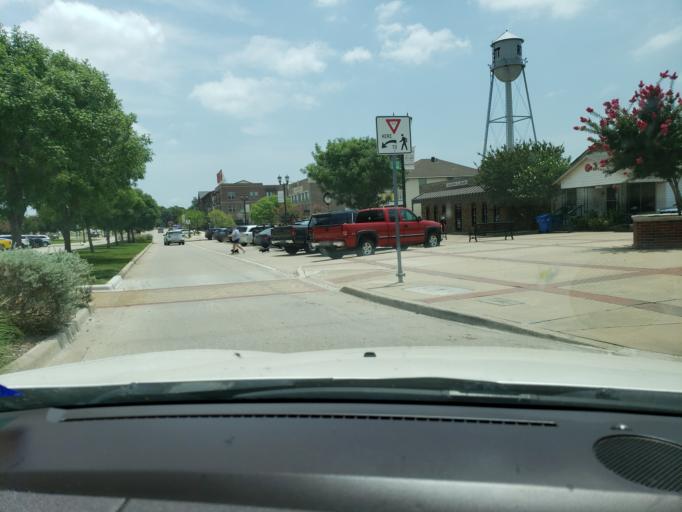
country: US
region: Texas
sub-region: Dallas County
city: Rowlett
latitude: 32.9029
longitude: -96.5664
